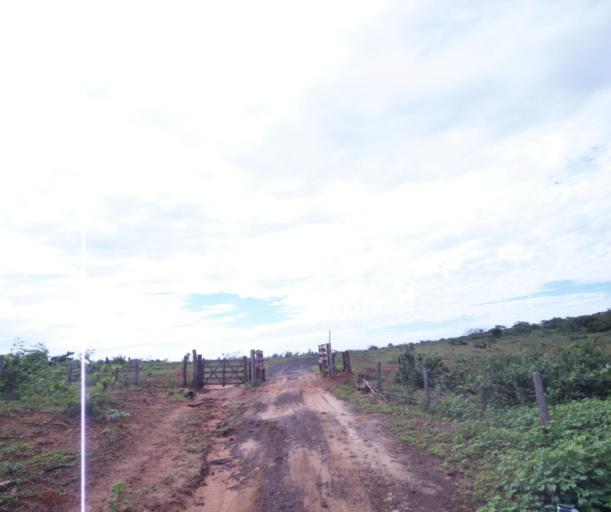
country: BR
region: Bahia
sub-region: Carinhanha
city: Carinhanha
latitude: -14.2196
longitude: -44.4419
